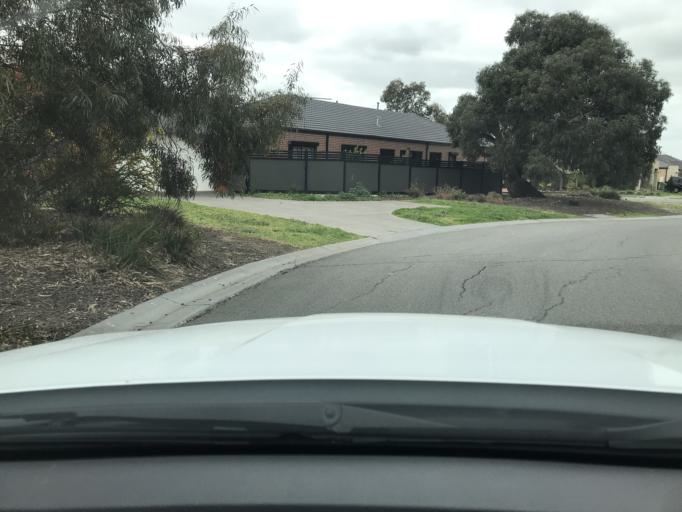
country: AU
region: Victoria
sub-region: Hume
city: Craigieburn
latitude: -37.5821
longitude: 144.9252
